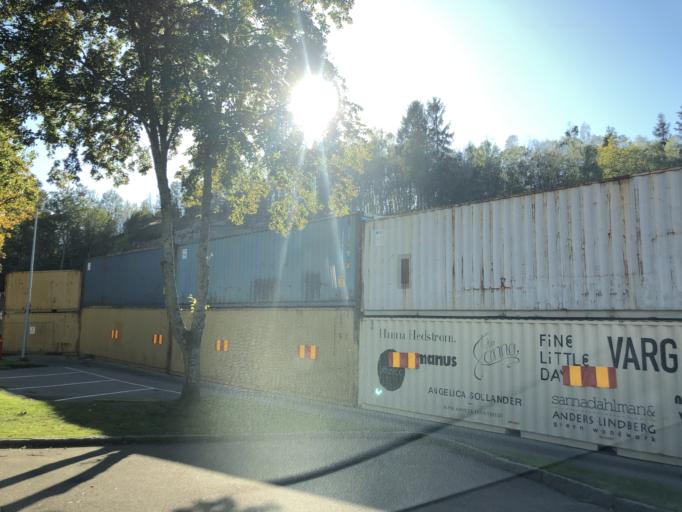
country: SE
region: Vaestra Goetaland
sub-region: Molndal
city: Moelndal
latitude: 57.6786
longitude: 12.0142
